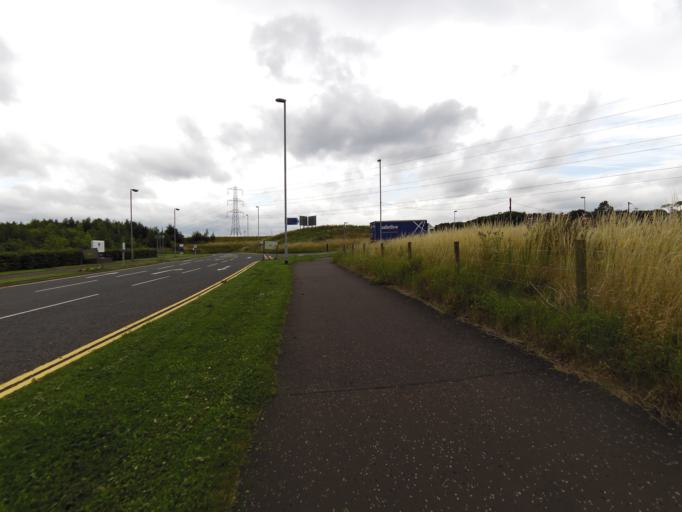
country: GB
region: Scotland
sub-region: East Lothian
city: Musselburgh
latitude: 55.9315
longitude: -3.0776
